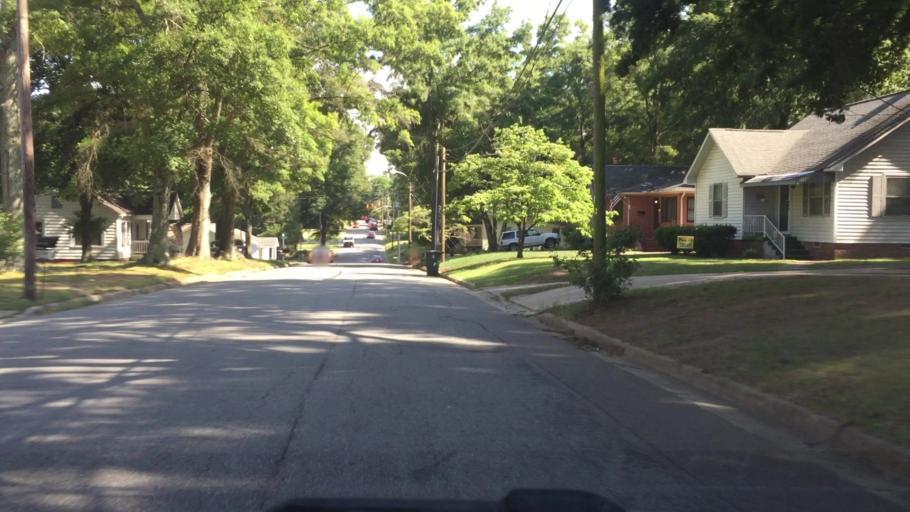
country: US
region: North Carolina
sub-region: Iredell County
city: Mooresville
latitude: 35.5851
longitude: -80.8001
